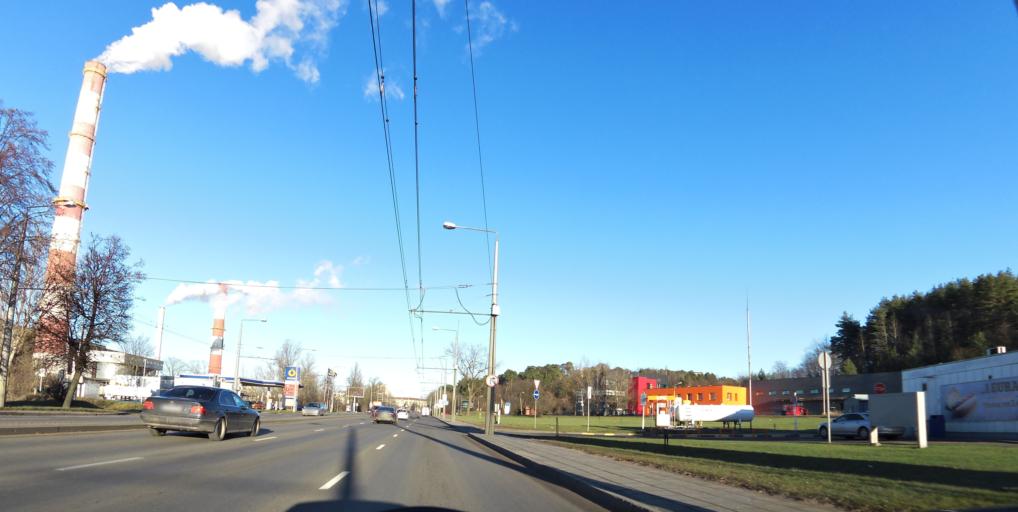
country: LT
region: Vilnius County
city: Vilkpede
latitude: 54.6617
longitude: 25.2348
